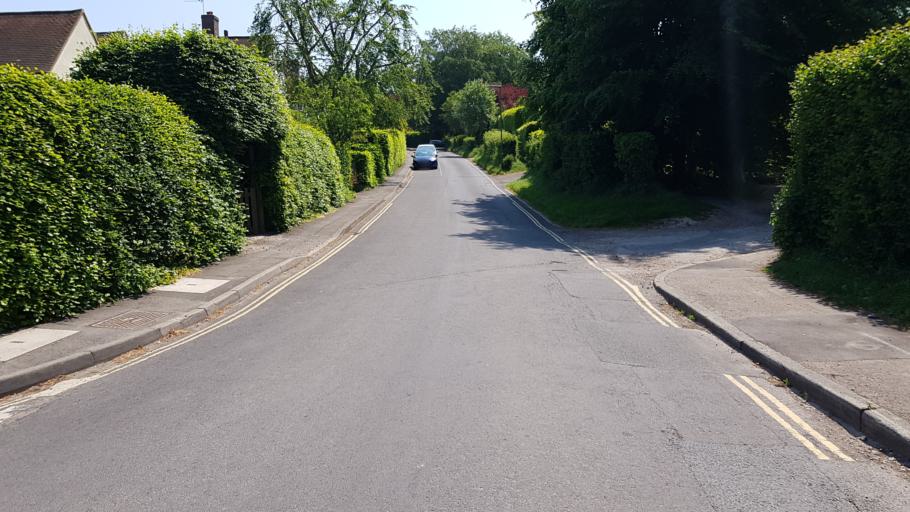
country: GB
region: England
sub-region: Surrey
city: Guildford
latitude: 51.2332
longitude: -0.5993
